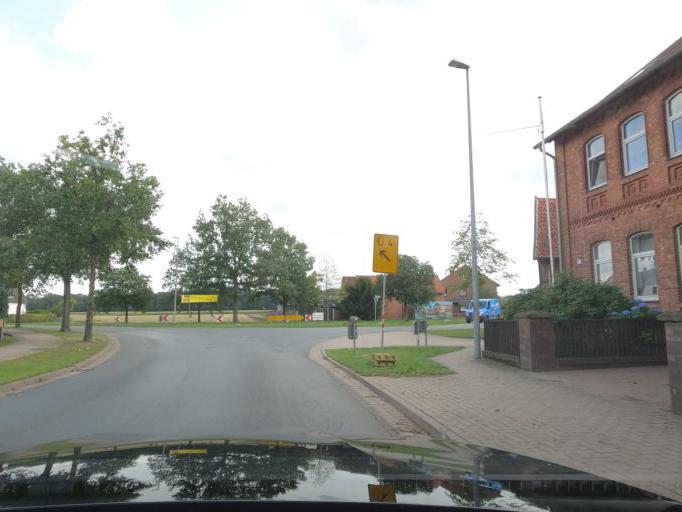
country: DE
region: Lower Saxony
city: Isernhagen Farster Bauerschaft
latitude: 52.5088
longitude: 9.8849
